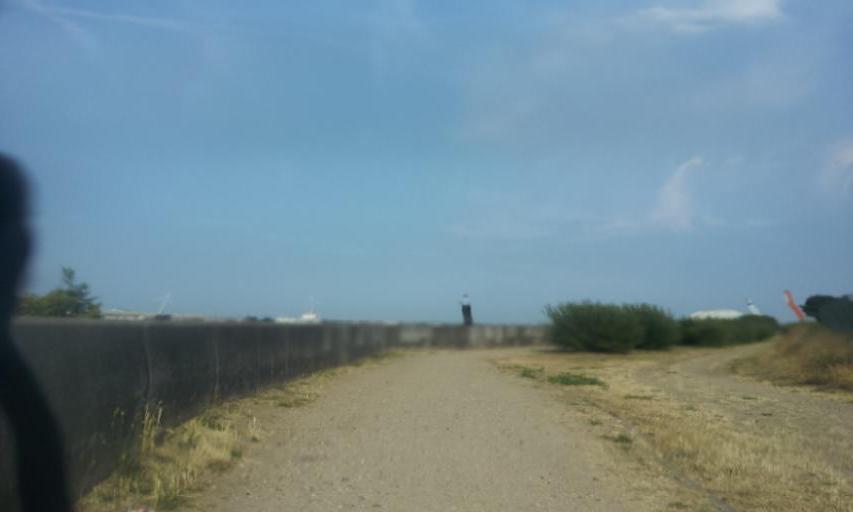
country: GB
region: England
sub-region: Greater London
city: Belvedere
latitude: 51.5107
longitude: 0.1352
